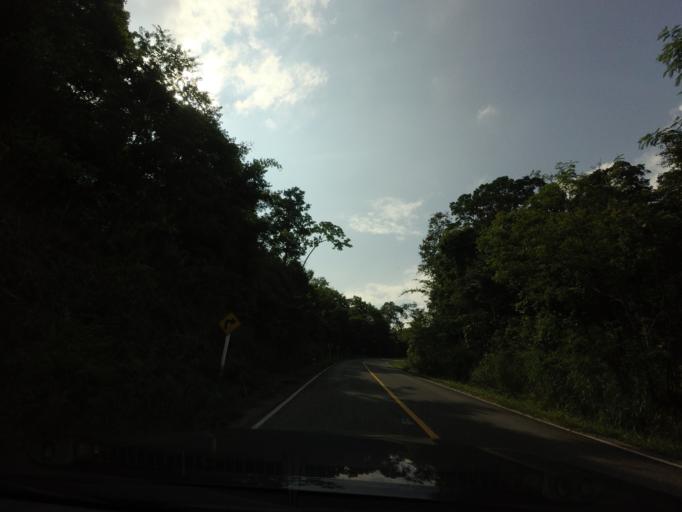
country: TH
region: Uttaradit
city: Ban Khok
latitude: 18.2423
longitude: 101.0069
